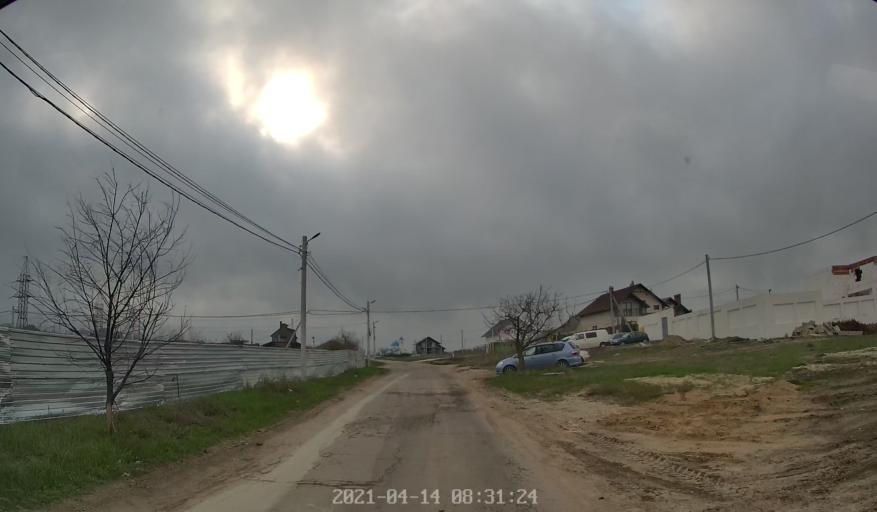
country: MD
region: Chisinau
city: Stauceni
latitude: 47.0613
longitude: 28.9344
